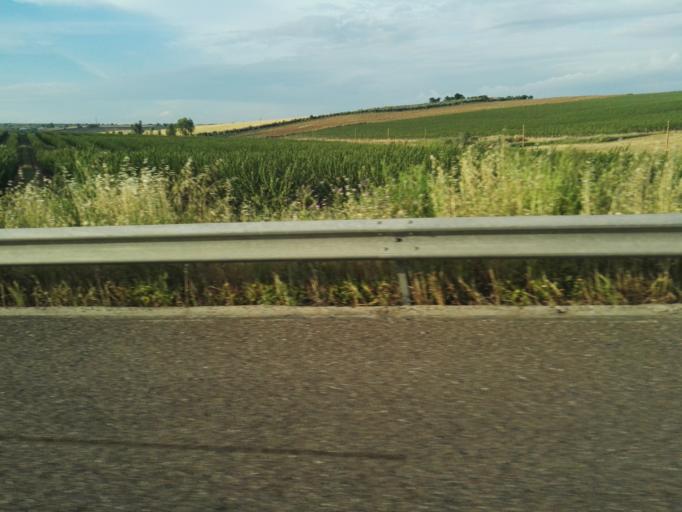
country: PT
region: Portalegre
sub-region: Elvas
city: Elvas
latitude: 38.8917
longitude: -7.1158
